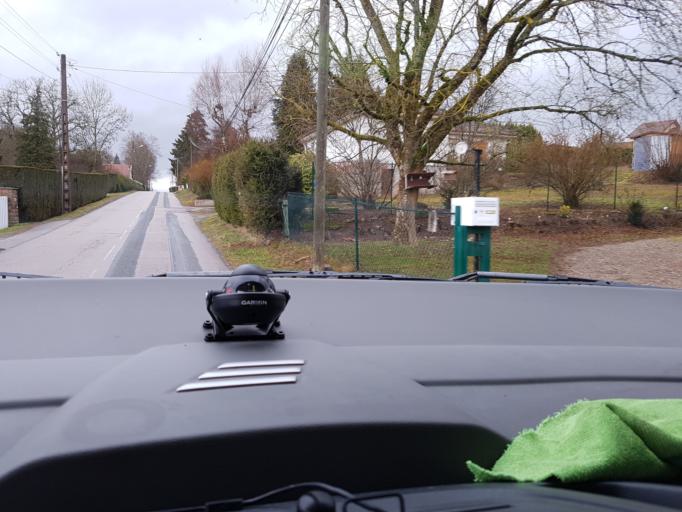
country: FR
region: Lorraine
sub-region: Departement des Vosges
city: Saint-Michel-sur-Meurthe
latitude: 48.3392
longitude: 6.8960
